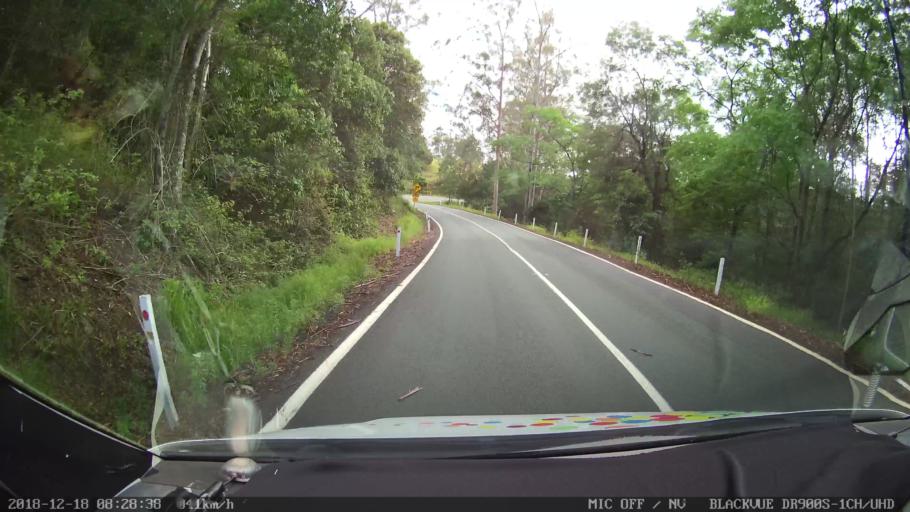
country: AU
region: New South Wales
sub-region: Kyogle
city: Kyogle
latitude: -28.3262
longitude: 152.7546
